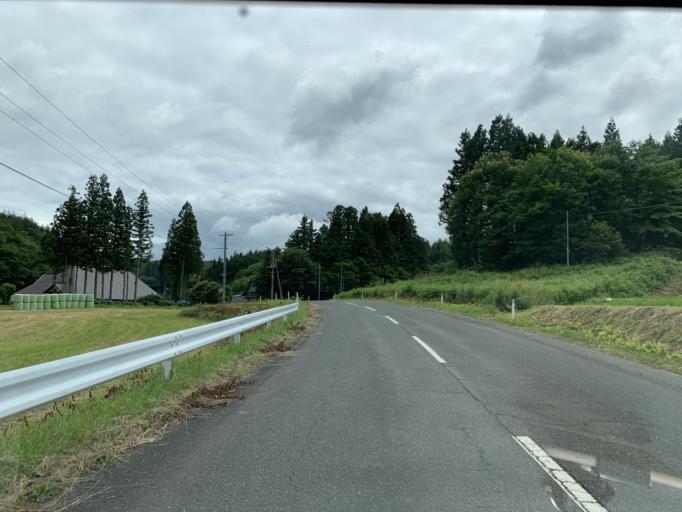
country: JP
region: Iwate
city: Ichinoseki
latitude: 38.9340
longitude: 140.9209
